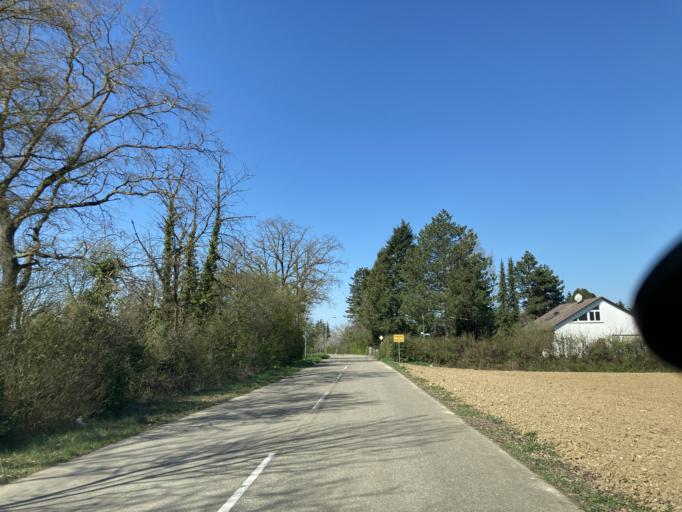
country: DE
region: Baden-Wuerttemberg
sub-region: Freiburg Region
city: Schliengen
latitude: 47.7639
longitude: 7.5587
